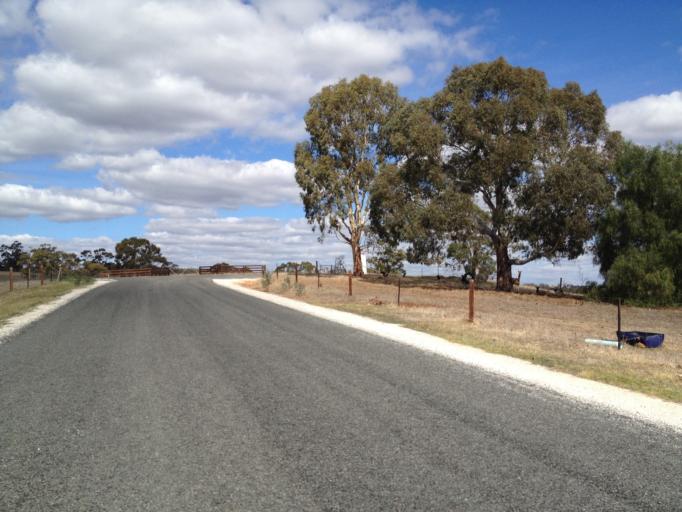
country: AU
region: South Australia
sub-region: Barossa
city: Lyndoch
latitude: -34.6309
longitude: 138.8310
